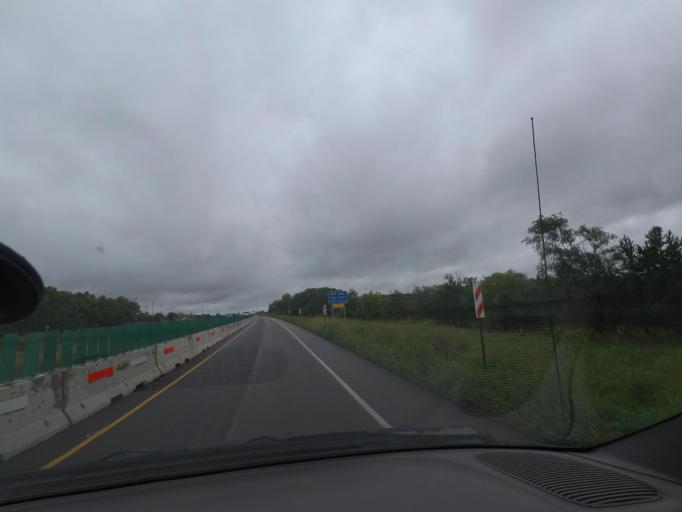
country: US
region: Illinois
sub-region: Piatt County
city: Cerro Gordo
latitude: 39.9842
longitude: -88.7890
